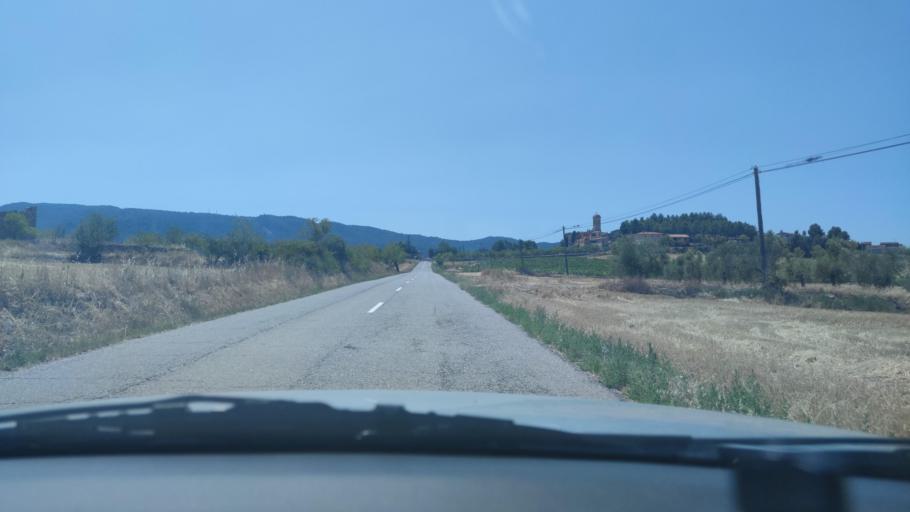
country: ES
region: Catalonia
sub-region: Provincia de Tarragona
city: Vallclara
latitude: 41.3879
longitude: 0.9495
